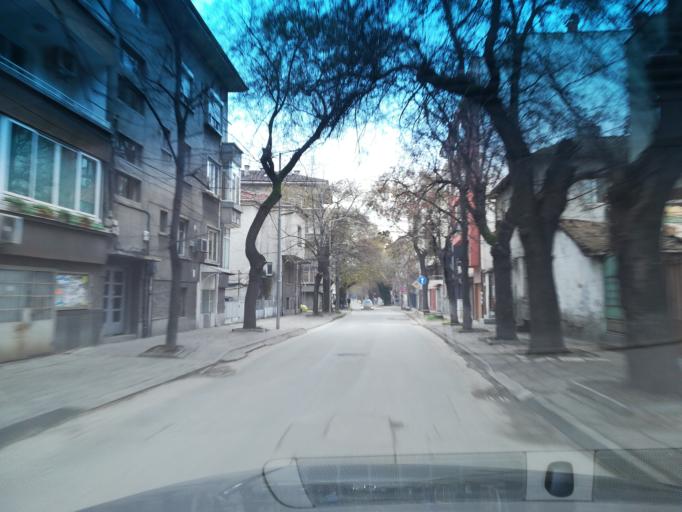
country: BG
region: Plovdiv
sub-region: Obshtina Plovdiv
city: Plovdiv
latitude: 42.1445
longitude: 24.7586
